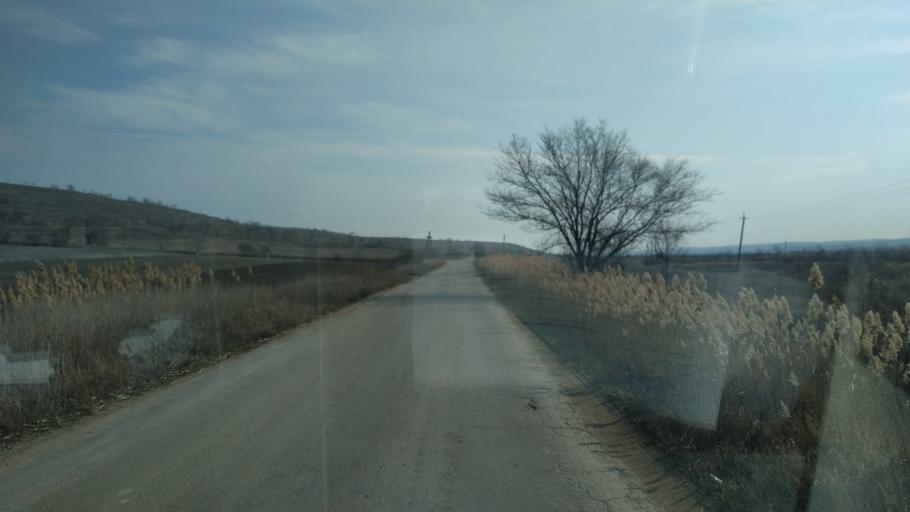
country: MD
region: Chisinau
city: Singera
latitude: 46.9252
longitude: 29.0800
